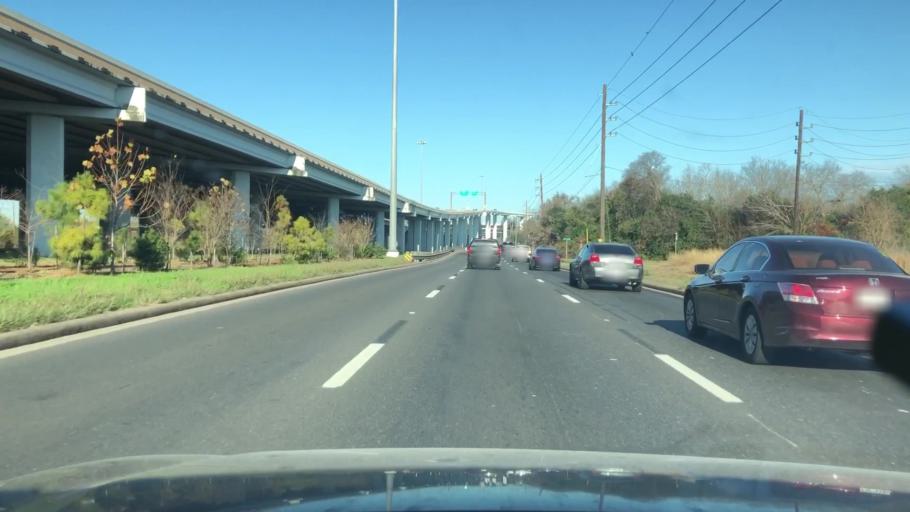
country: US
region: Texas
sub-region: Fort Bend County
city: Meadows Place
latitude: 29.6556
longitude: -95.5518
